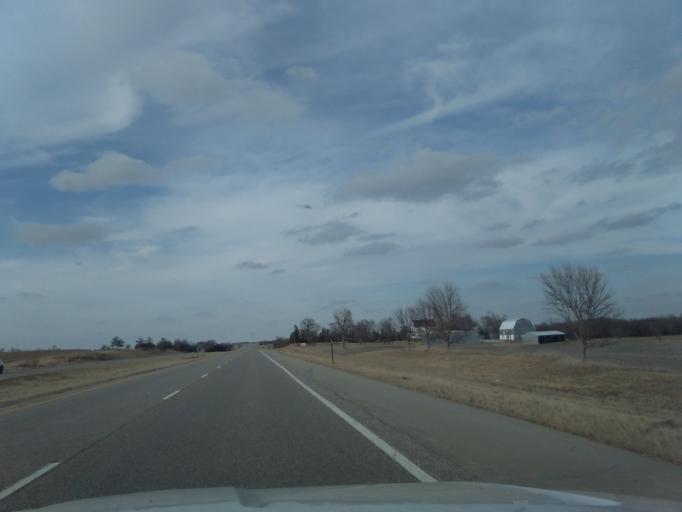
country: US
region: Nebraska
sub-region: Gage County
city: Beatrice
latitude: 40.4226
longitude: -96.7422
